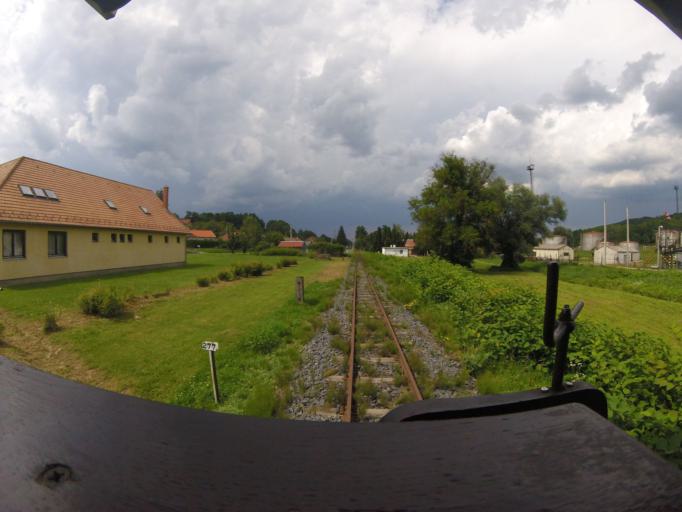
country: HU
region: Zala
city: Letenye
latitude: 46.5133
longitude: 16.7297
